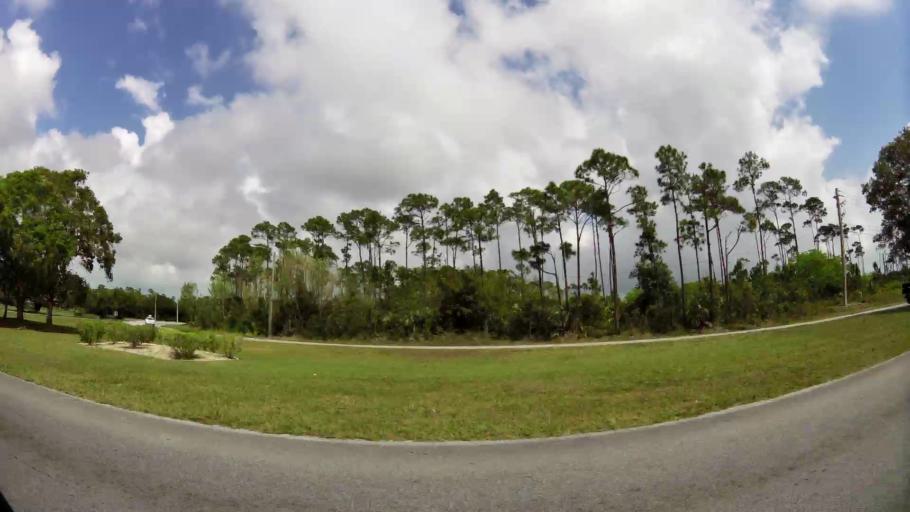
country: BS
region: Freeport
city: Lucaya
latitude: 26.5229
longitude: -78.6592
